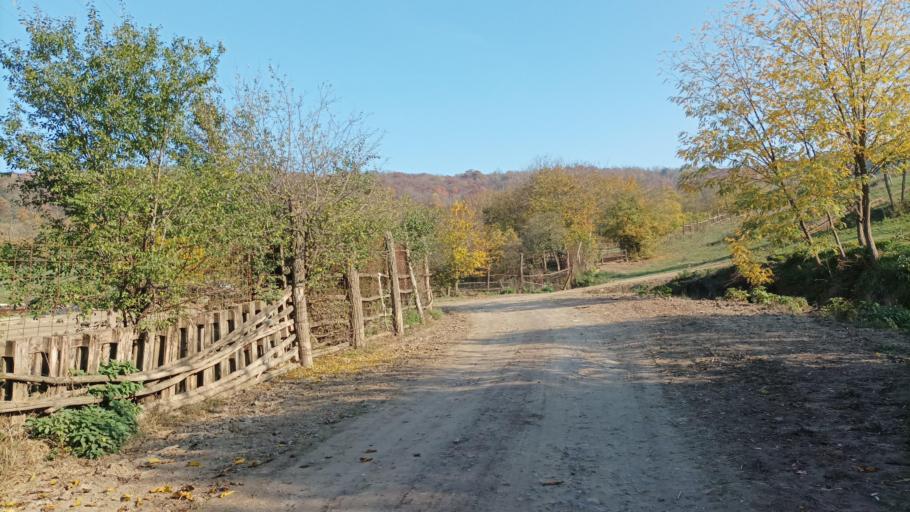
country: HU
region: Tolna
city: Szentgalpuszta
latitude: 46.3393
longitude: 18.6033
